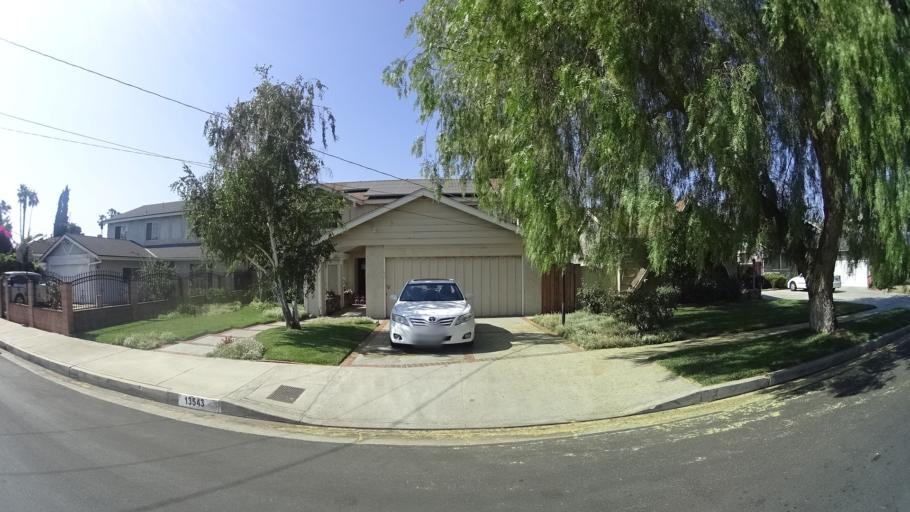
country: US
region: California
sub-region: Los Angeles County
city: Van Nuys
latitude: 34.1967
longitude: -118.4284
